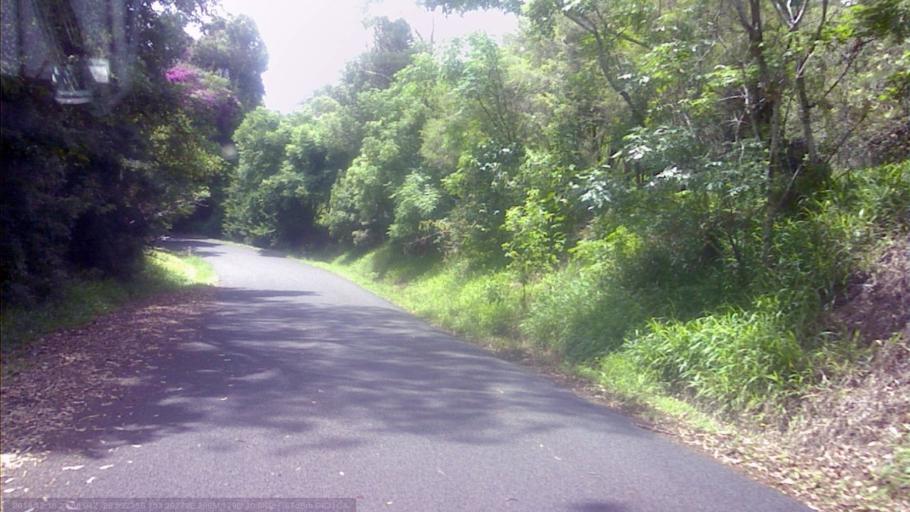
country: AU
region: New South Wales
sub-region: Lismore Municipality
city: Nimbin
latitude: -28.5923
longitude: 153.2628
